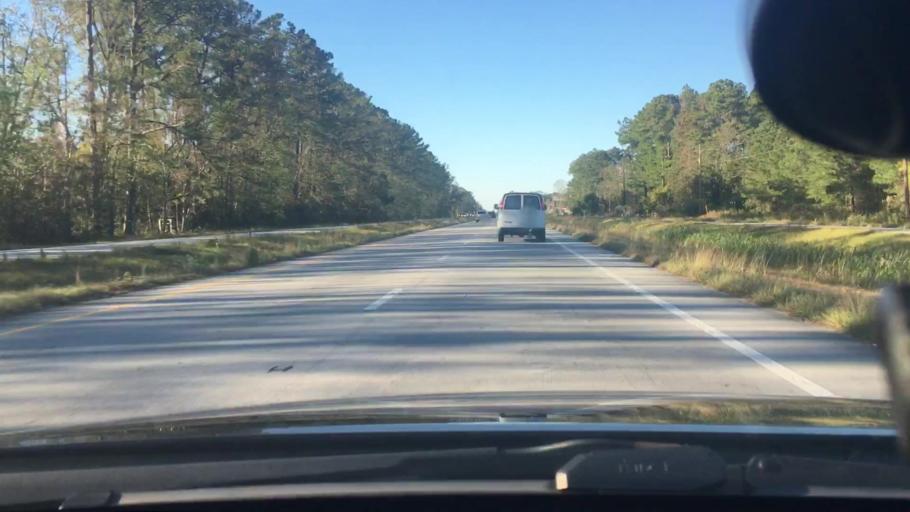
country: US
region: North Carolina
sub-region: Craven County
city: Fairfield Harbour
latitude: 35.0328
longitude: -77.0042
